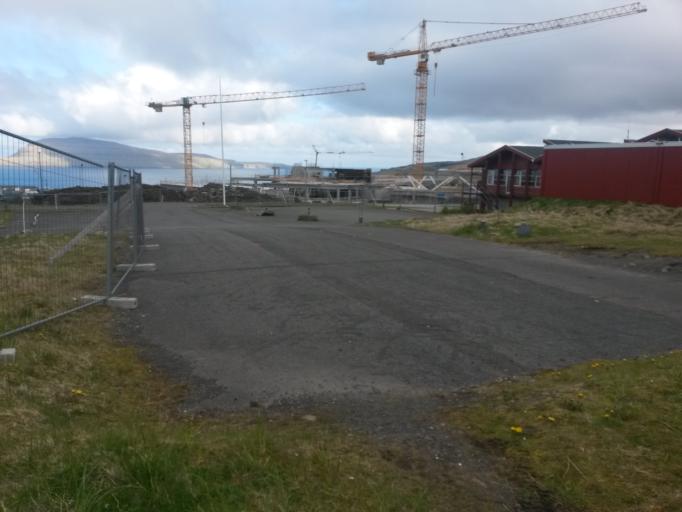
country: FO
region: Streymoy
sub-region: Torshavn
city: Torshavn
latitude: 62.0070
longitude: -6.8015
